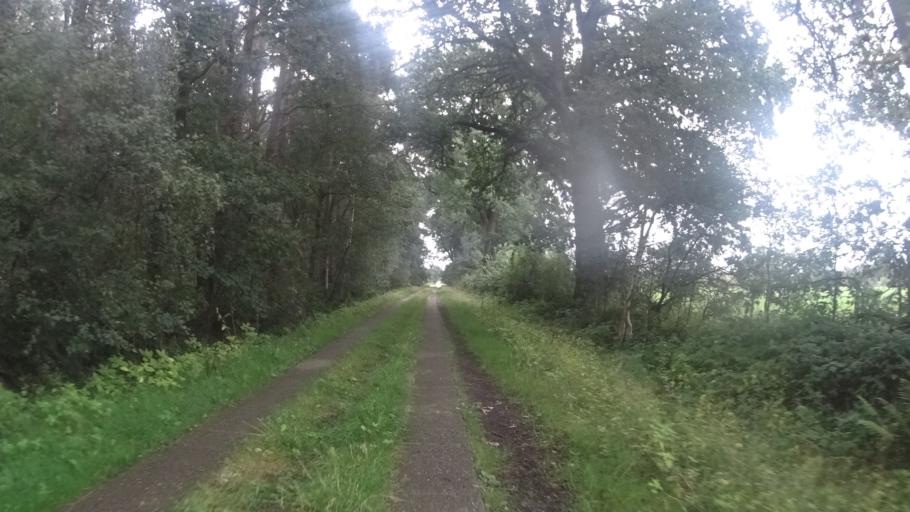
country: DE
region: Schleswig-Holstein
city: Heede
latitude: 53.7616
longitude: 9.7946
